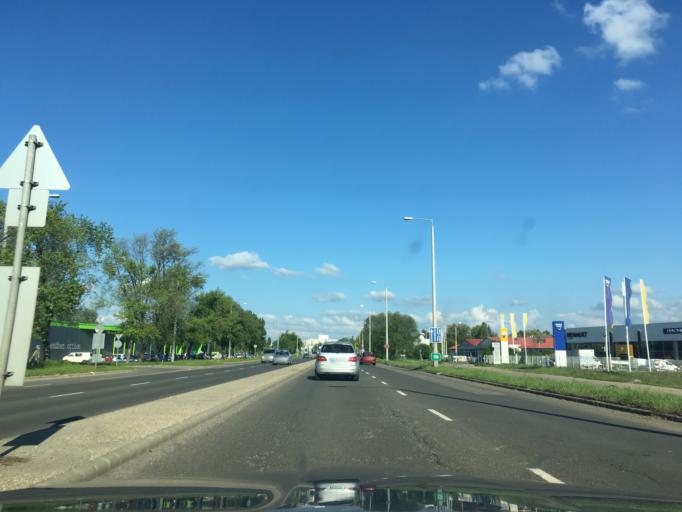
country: HU
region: Hajdu-Bihar
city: Debrecen
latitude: 47.5434
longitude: 21.5883
